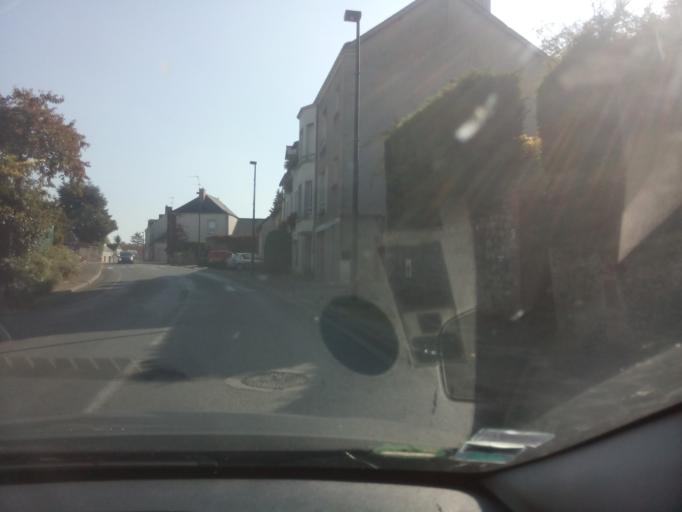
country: FR
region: Pays de la Loire
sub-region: Departement de Maine-et-Loire
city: Seiches-sur-le-Loir
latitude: 47.5759
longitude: -0.3638
